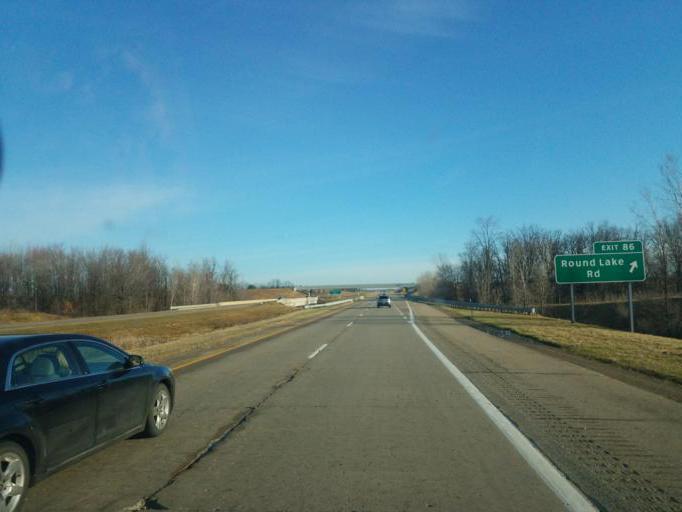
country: US
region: Michigan
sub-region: Clinton County
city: DeWitt
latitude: 42.8528
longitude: -84.5185
